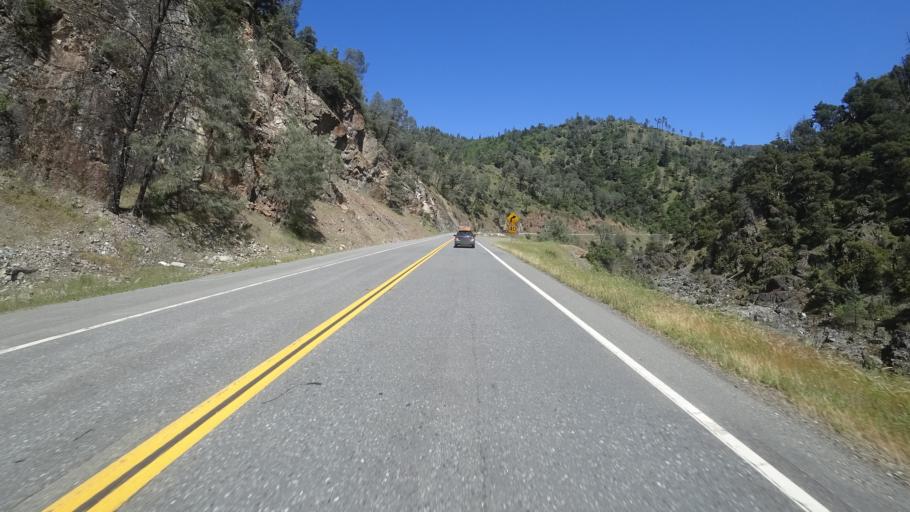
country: US
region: California
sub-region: Humboldt County
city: Willow Creek
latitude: 40.7941
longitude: -123.3696
